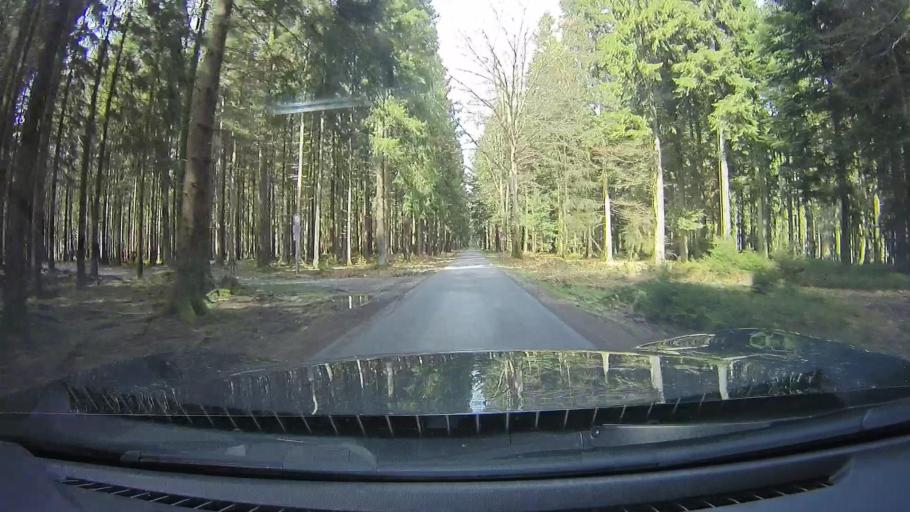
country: DE
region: Hesse
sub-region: Regierungsbezirk Darmstadt
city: Hesseneck
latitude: 49.5975
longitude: 9.0838
